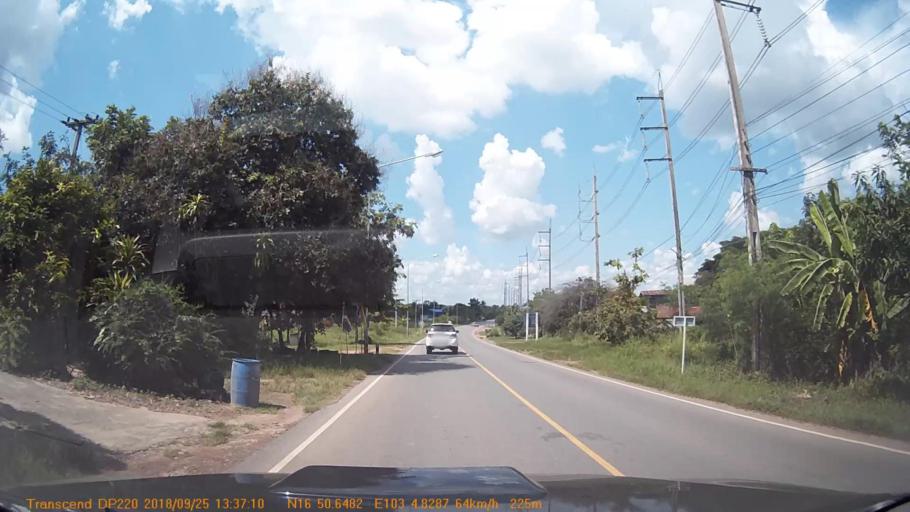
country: TH
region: Khon Kaen
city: Kranuan
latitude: 16.8442
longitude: 103.0805
